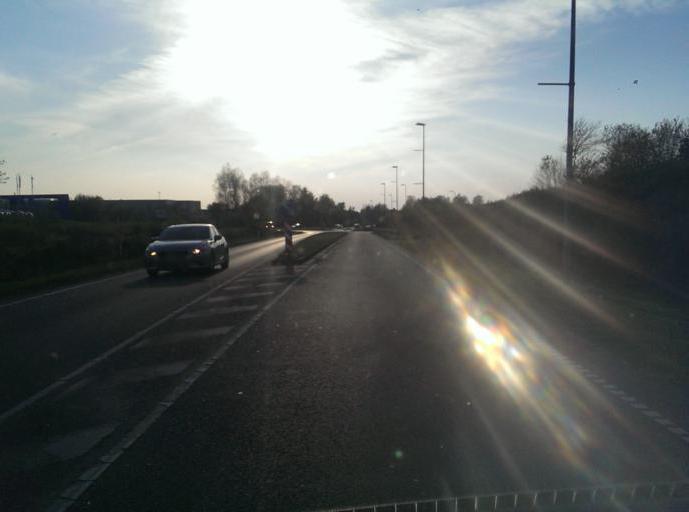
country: DK
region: South Denmark
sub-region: Esbjerg Kommune
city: Esbjerg
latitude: 55.5176
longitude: 8.4713
